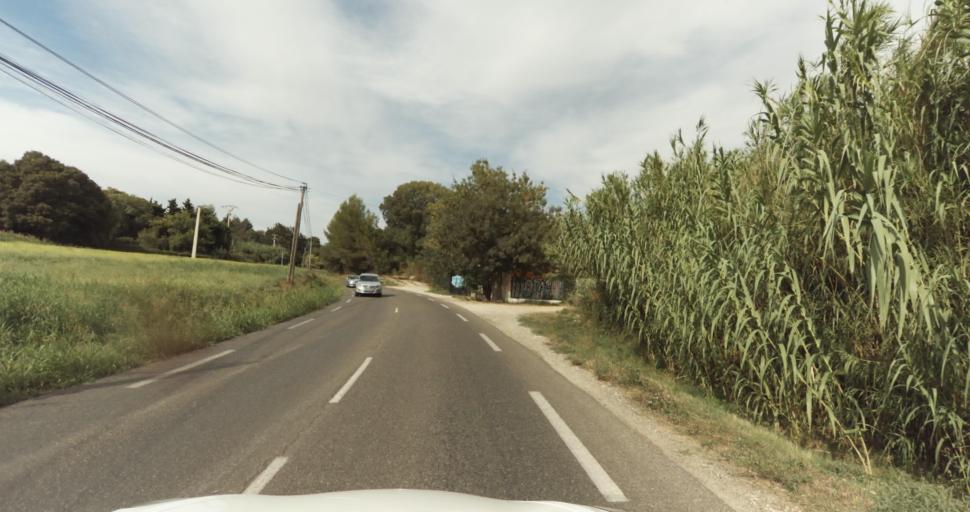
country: FR
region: Provence-Alpes-Cote d'Azur
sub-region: Departement des Bouches-du-Rhone
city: Saint-Chamas
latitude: 43.5577
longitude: 5.0144
